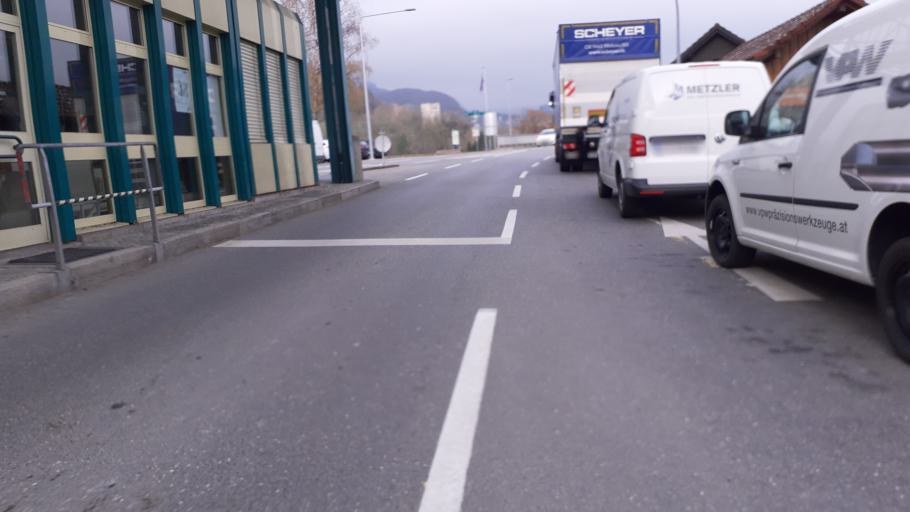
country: AT
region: Vorarlberg
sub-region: Politischer Bezirk Feldkirch
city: Meiningen
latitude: 47.3044
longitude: 9.5724
